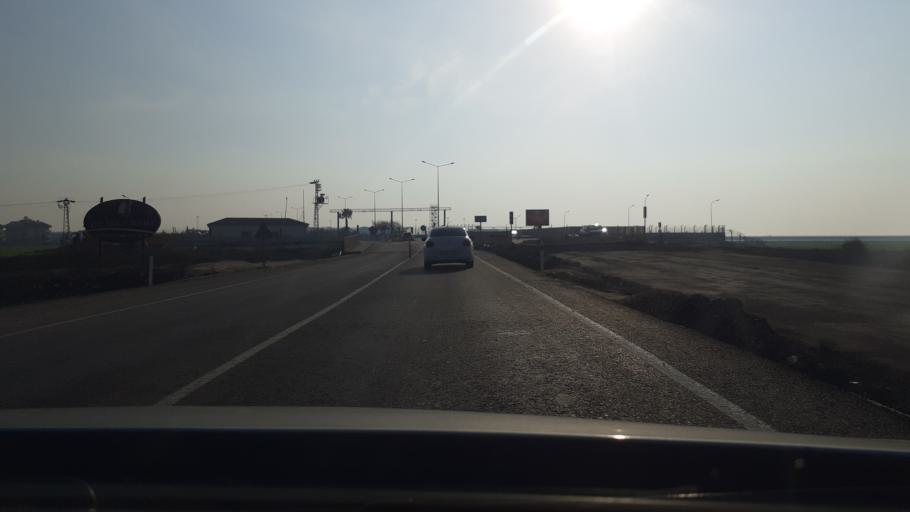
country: TR
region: Hatay
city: Serinyol
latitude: 36.3648
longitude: 36.2719
